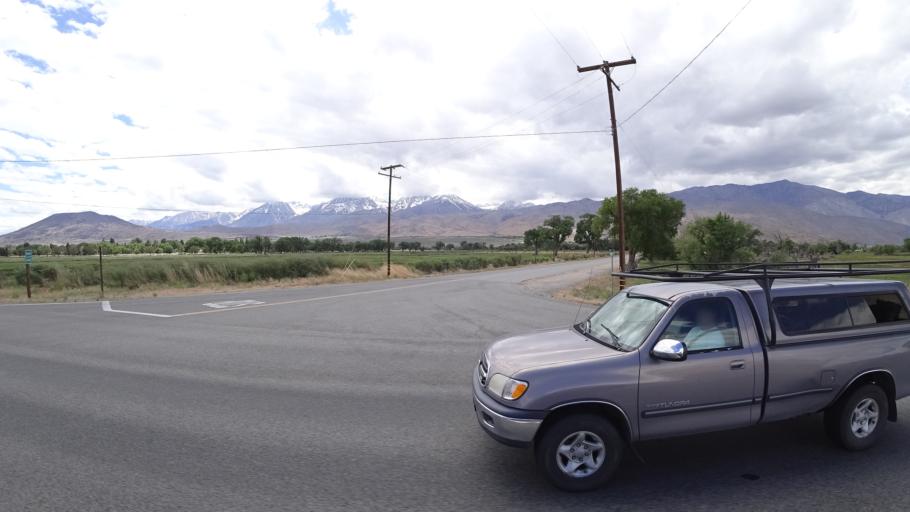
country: US
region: California
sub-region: Inyo County
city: Big Pine
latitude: 37.1737
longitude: -118.2905
